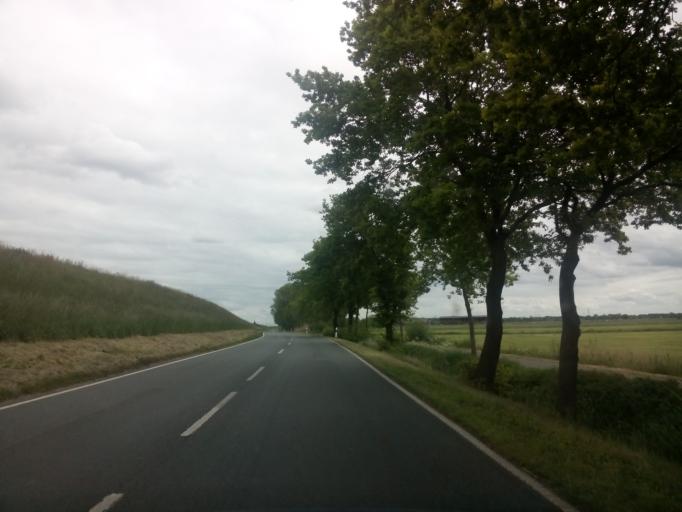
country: DE
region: Lower Saxony
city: Lemwerder
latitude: 53.1241
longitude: 8.6332
